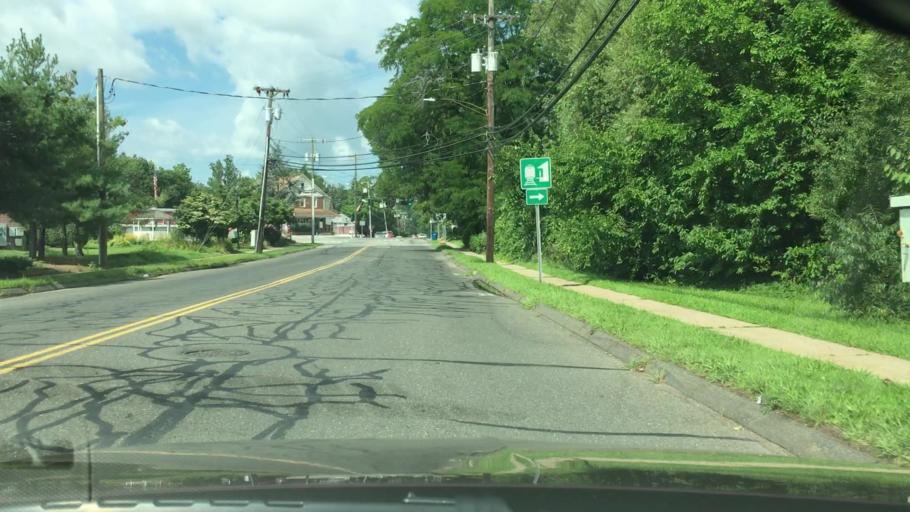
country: US
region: Connecticut
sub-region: Hartford County
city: Kensington
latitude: 41.6317
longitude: -72.7595
